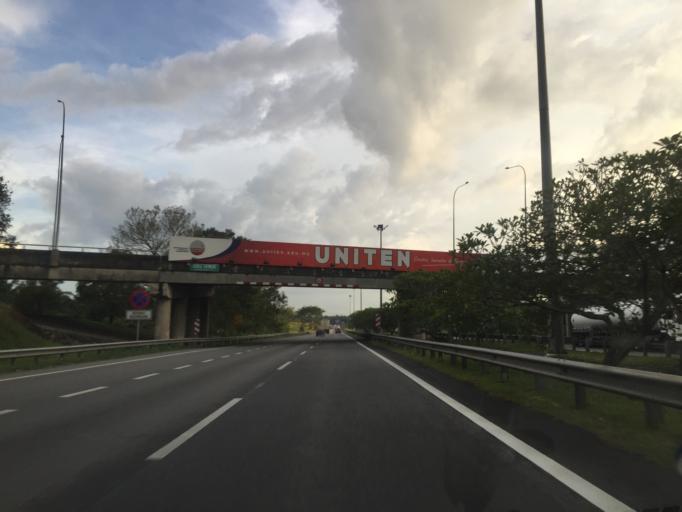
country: MY
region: Kedah
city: Gurun
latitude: 5.8128
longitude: 100.4914
